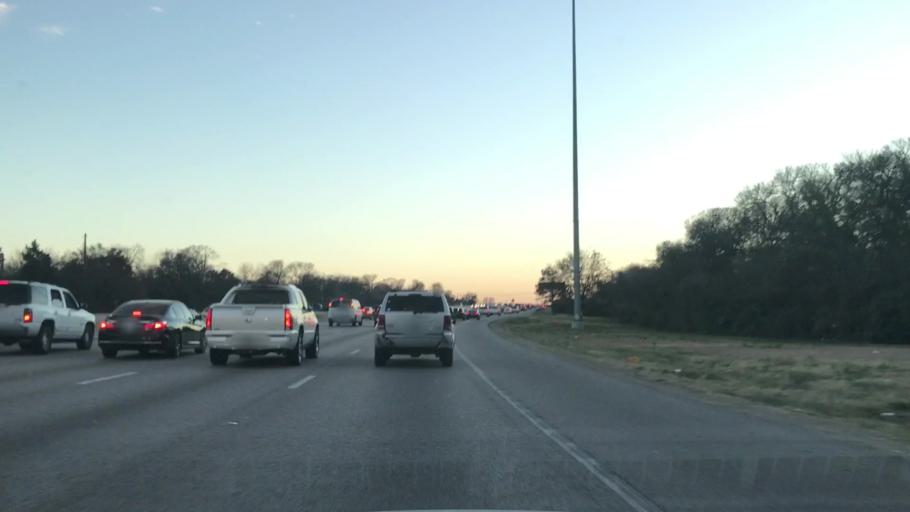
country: US
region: Texas
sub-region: Dallas County
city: Dallas
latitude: 32.7285
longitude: -96.8258
